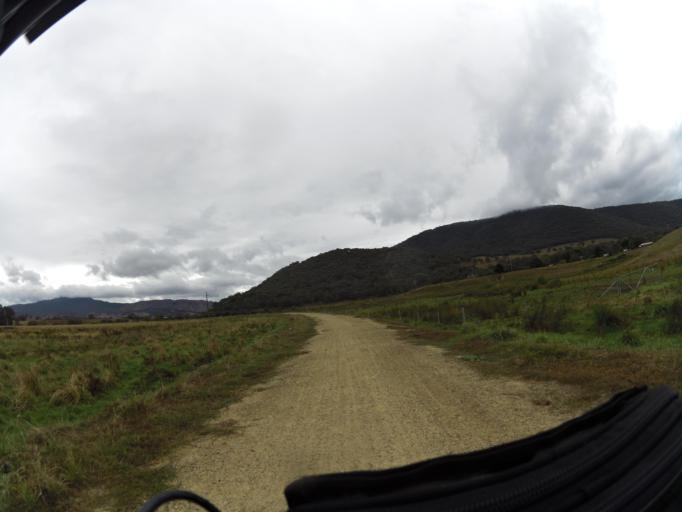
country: AU
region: New South Wales
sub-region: Albury Municipality
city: East Albury
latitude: -36.1816
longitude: 147.3460
